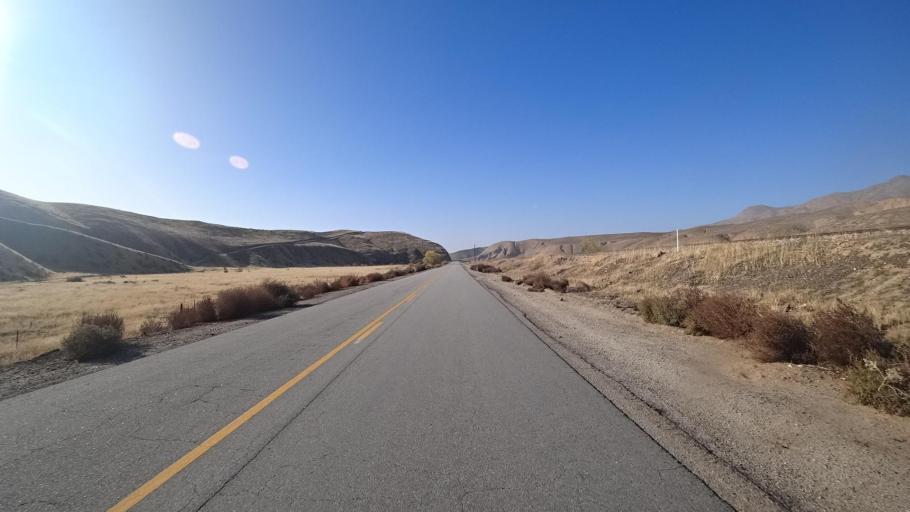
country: US
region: California
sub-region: Kern County
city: Arvin
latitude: 35.3212
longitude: -118.7094
